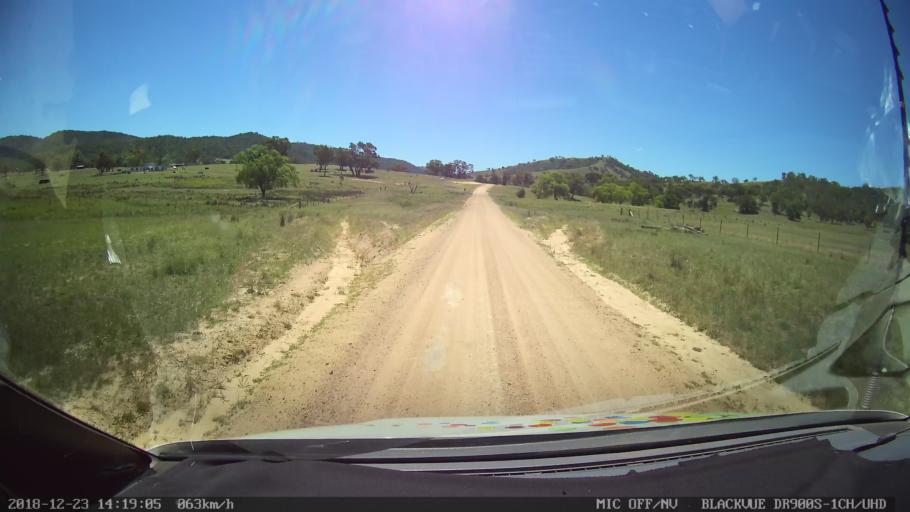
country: AU
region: New South Wales
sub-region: Tamworth Municipality
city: Manilla
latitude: -30.6546
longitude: 150.9989
